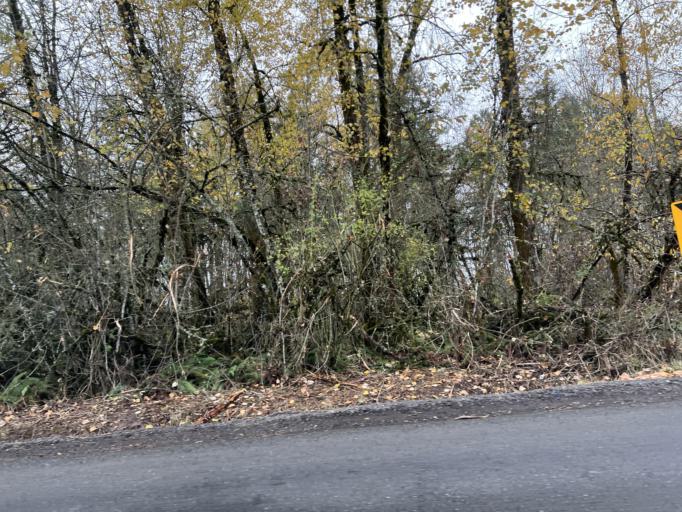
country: US
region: Oregon
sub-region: Polk County
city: Independence
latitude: 44.8058
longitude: -123.0891
